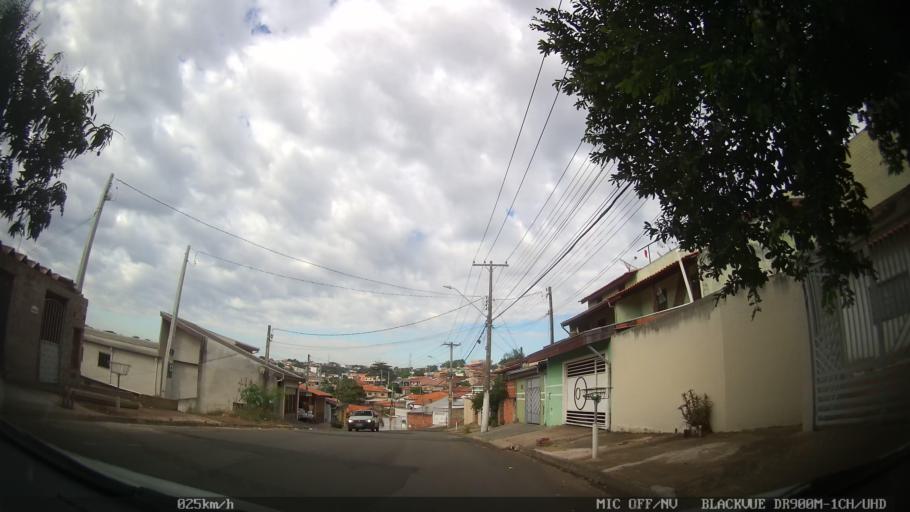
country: BR
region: Sao Paulo
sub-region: Americana
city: Americana
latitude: -22.7233
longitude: -47.3556
